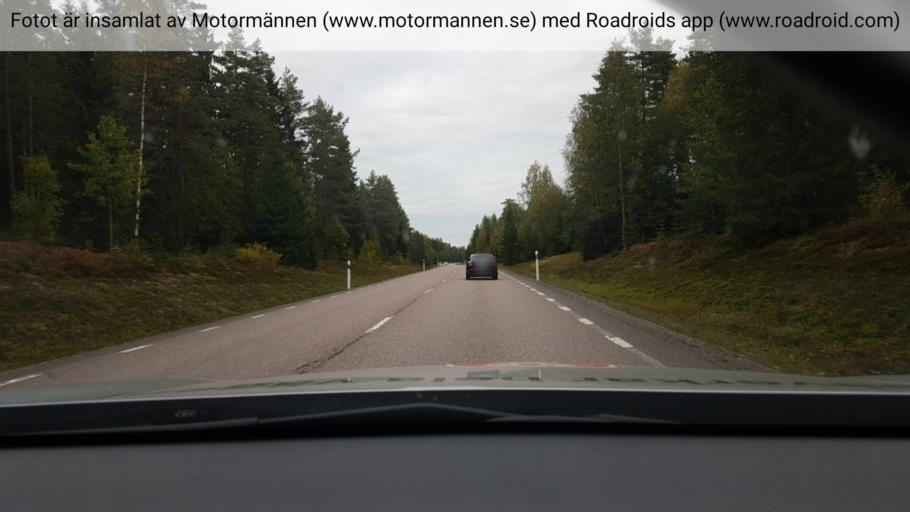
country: SE
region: Gaevleborg
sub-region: Gavle Kommun
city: Hedesunda
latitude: 60.3659
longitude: 16.9694
